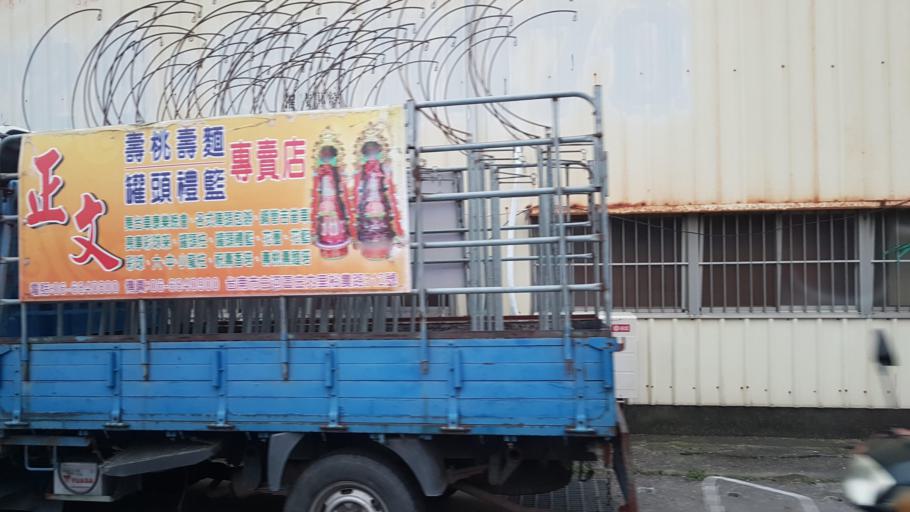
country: TW
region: Taiwan
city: Xinying
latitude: 23.3555
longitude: 120.4194
